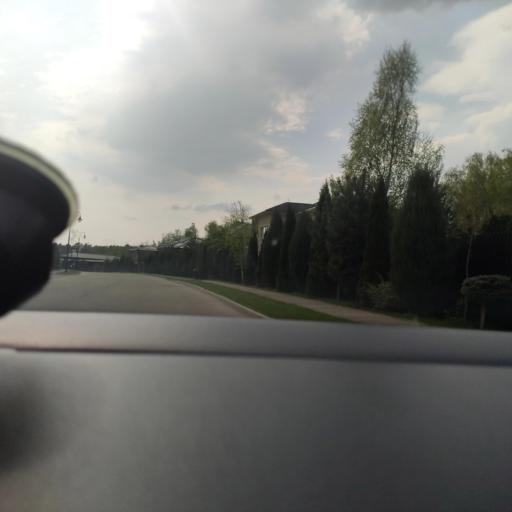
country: RU
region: Moskovskaya
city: Nakhabino
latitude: 55.8239
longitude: 37.1417
